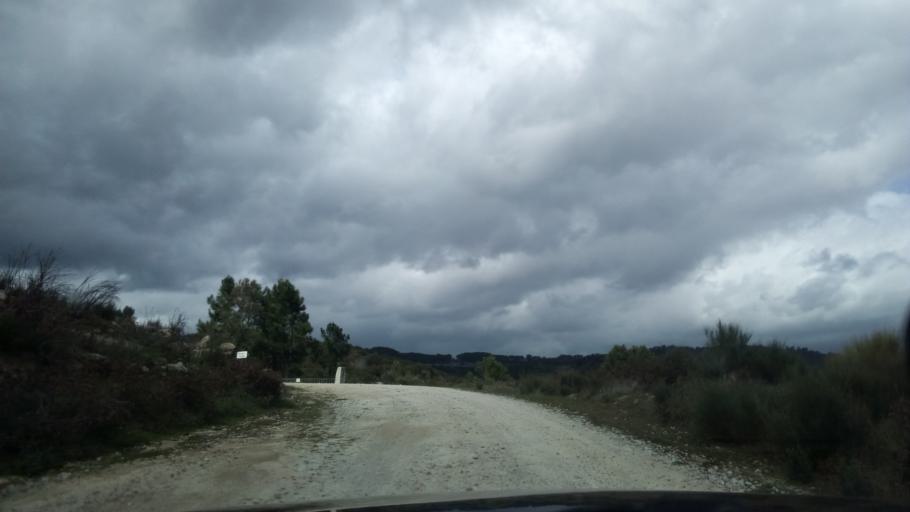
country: PT
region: Guarda
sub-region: Fornos de Algodres
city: Fornos de Algodres
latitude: 40.5925
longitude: -7.5672
